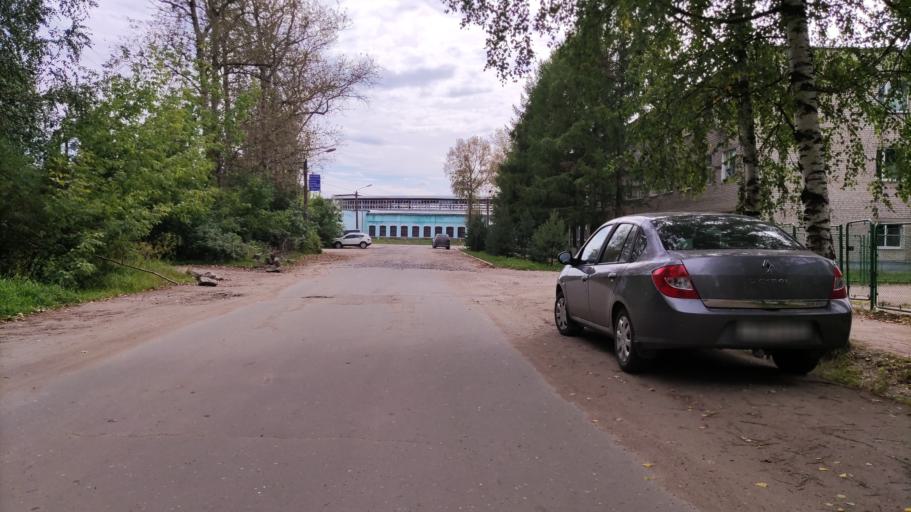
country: RU
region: Tverskaya
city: Rzhev
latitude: 56.2418
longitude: 34.3299
